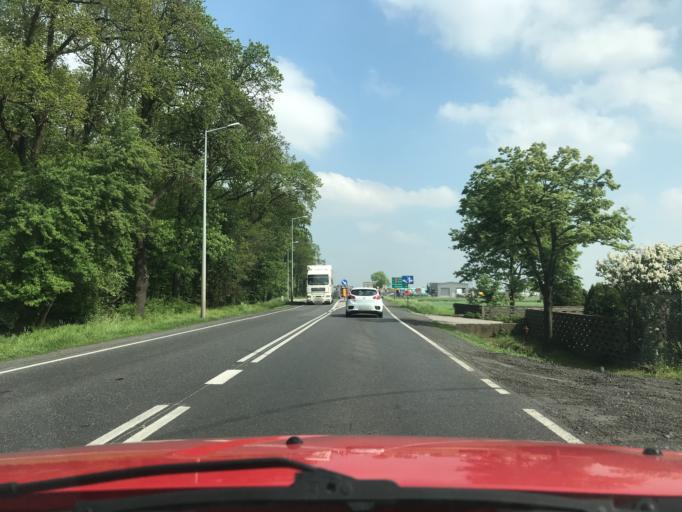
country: PL
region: Greater Poland Voivodeship
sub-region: Powiat pleszewski
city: Czermin
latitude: 51.9062
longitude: 17.7343
